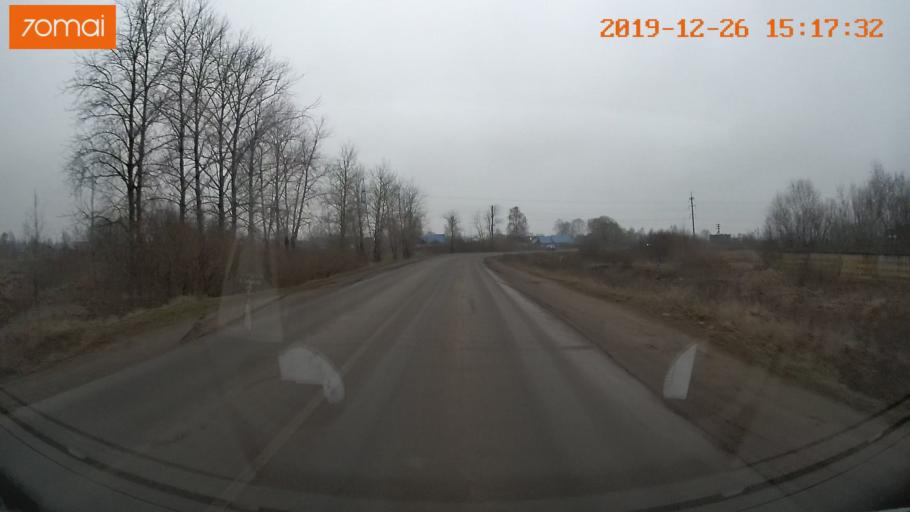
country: RU
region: Jaroslavl
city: Rybinsk
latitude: 58.0762
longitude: 38.8507
